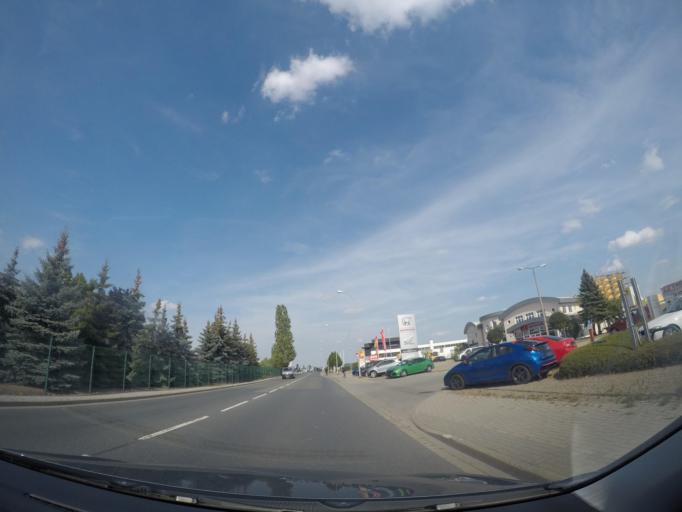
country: DE
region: Saxony-Anhalt
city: Wernigerode
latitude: 51.8482
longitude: 10.7852
